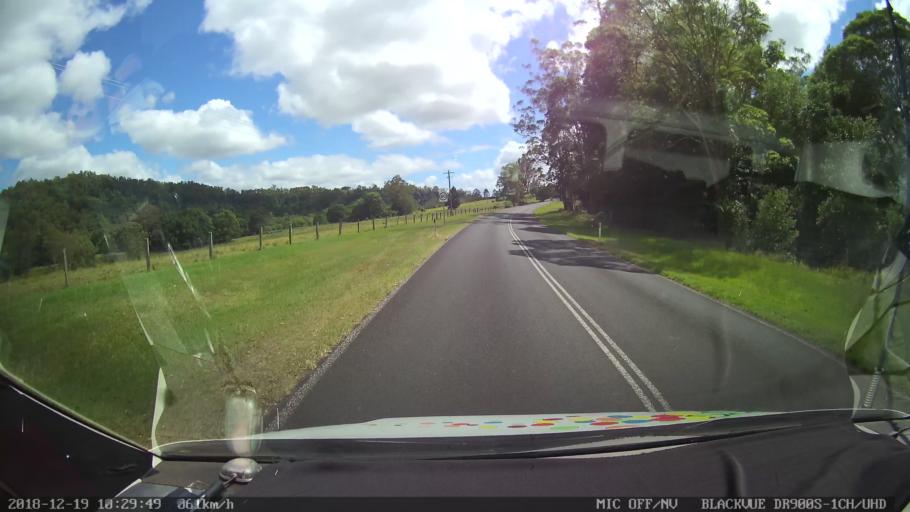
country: AU
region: New South Wales
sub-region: Lismore Municipality
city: Larnook
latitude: -28.5930
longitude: 153.1020
